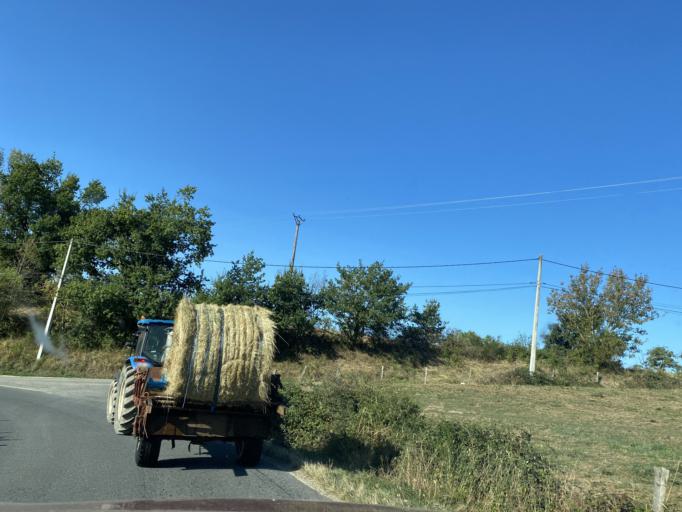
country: FR
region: Auvergne
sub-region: Departement du Puy-de-Dome
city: Escoutoux
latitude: 45.8120
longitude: 3.5853
